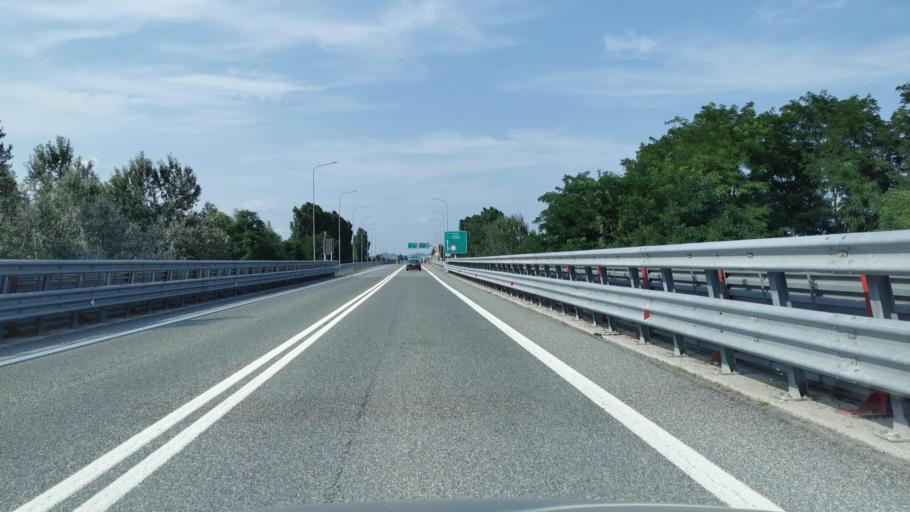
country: IT
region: Piedmont
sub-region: Provincia di Cuneo
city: Cherasco
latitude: 44.6590
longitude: 7.8703
